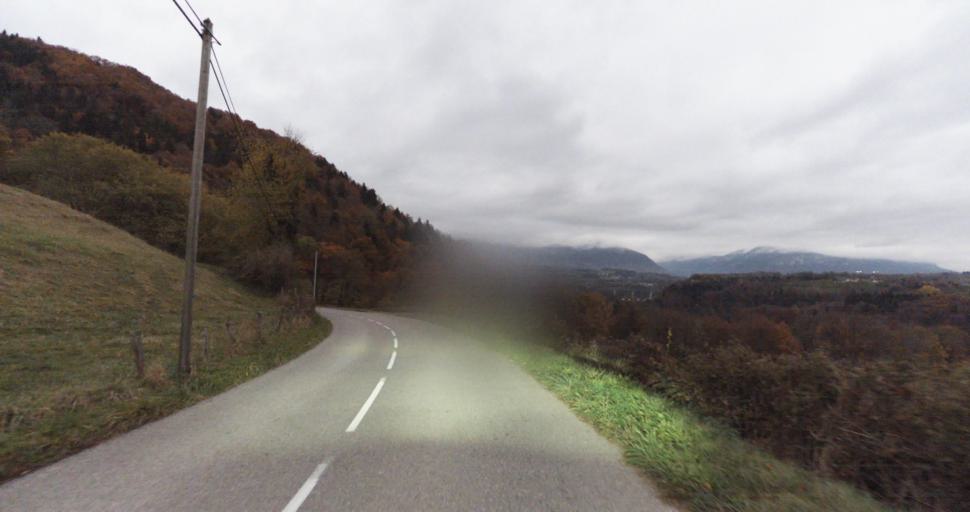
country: FR
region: Rhone-Alpes
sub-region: Departement de la Haute-Savoie
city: Alby-sur-Cheran
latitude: 45.8344
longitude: 6.0116
